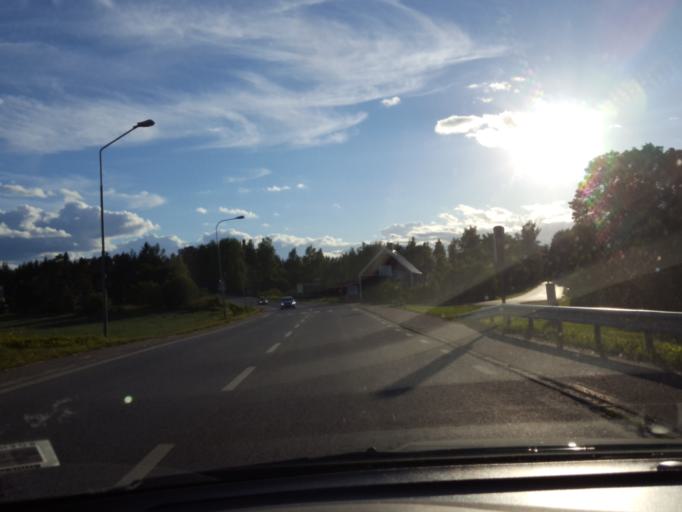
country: SE
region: Uppsala
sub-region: Osthammars Kommun
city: Gimo
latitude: 60.2166
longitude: 18.2056
